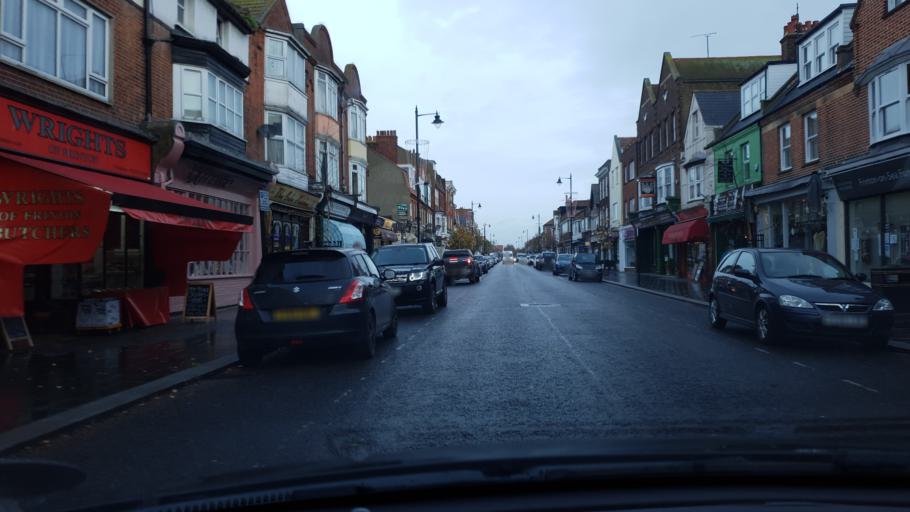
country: GB
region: England
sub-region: Essex
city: Frinton-on-Sea
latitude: 51.8311
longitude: 1.2456
